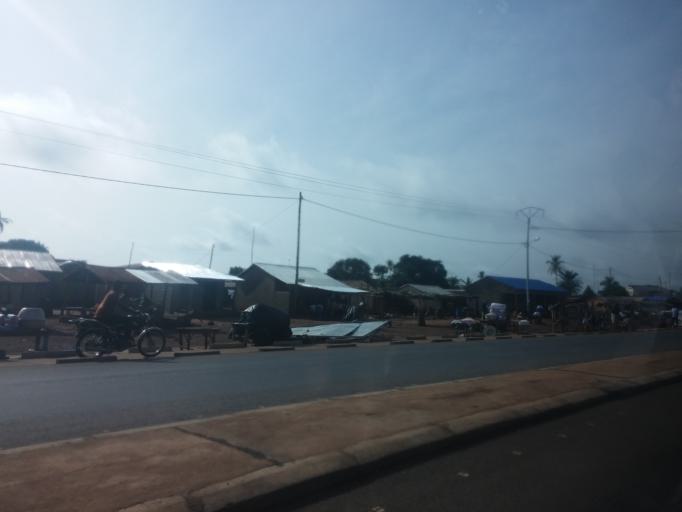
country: TG
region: Centrale
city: Sotouboua
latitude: 8.3446
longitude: 1.0092
